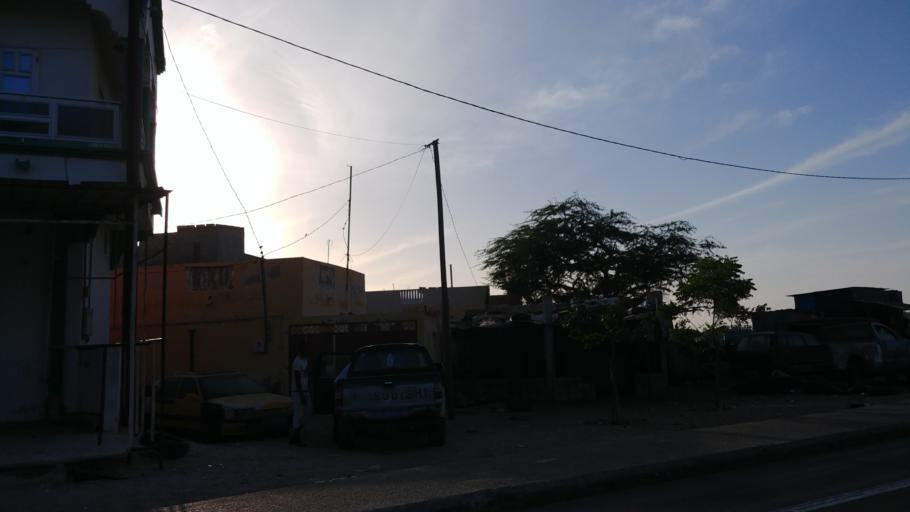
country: SN
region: Saint-Louis
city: Saint-Louis
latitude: 16.0118
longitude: -16.4961
